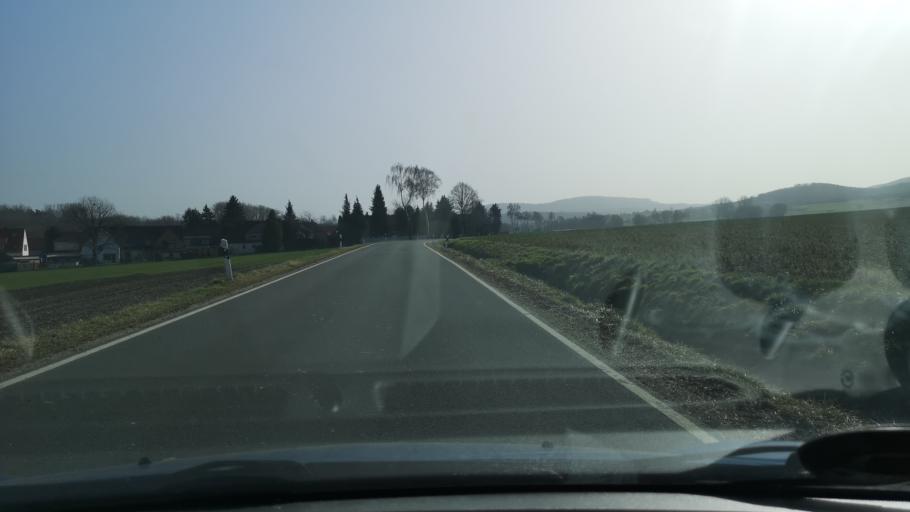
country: DE
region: Lower Saxony
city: Weenzen
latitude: 52.0140
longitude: 9.6286
